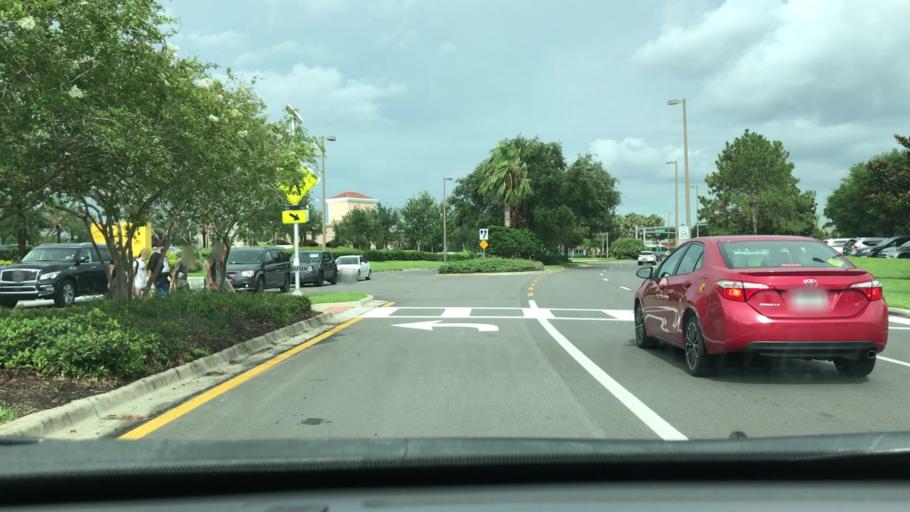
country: US
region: Florida
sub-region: Orange County
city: Williamsburg
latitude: 28.3895
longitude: -81.4920
